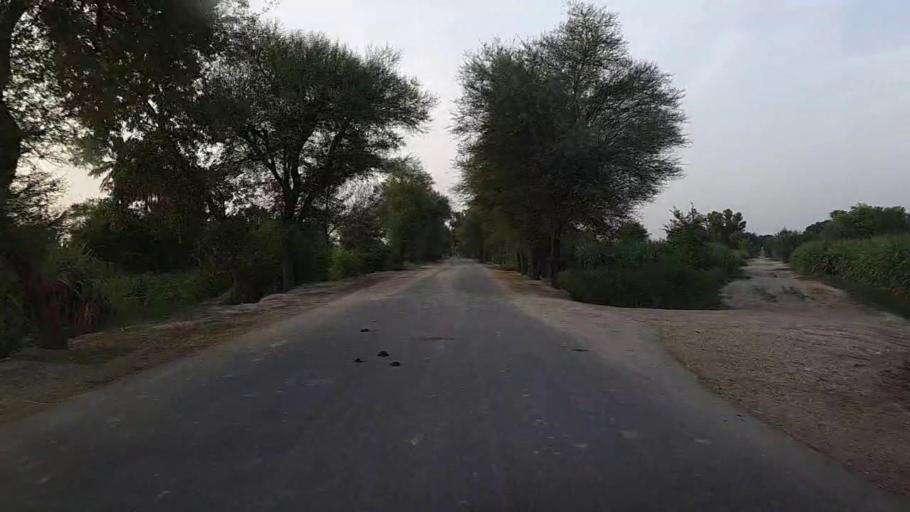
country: PK
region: Sindh
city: Ubauro
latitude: 28.2869
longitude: 69.8002
